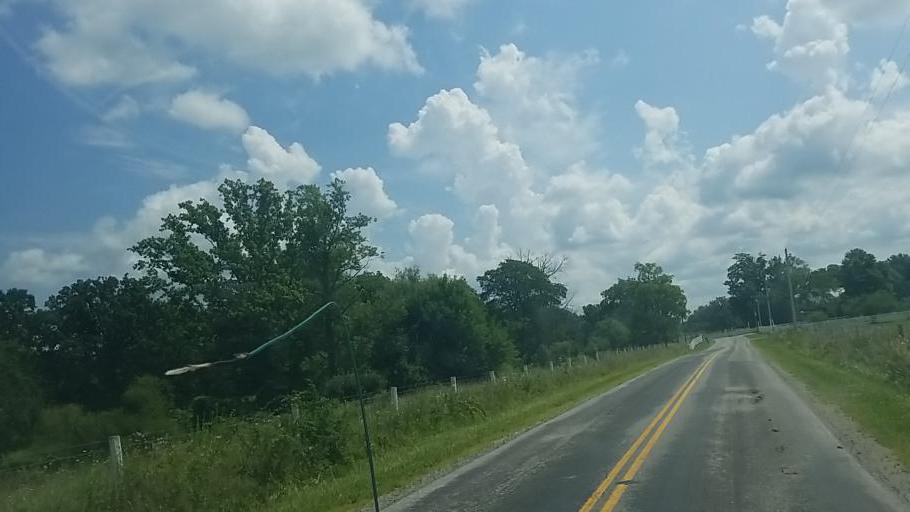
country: US
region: Ohio
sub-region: Wayne County
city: West Salem
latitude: 41.0409
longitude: -82.1400
